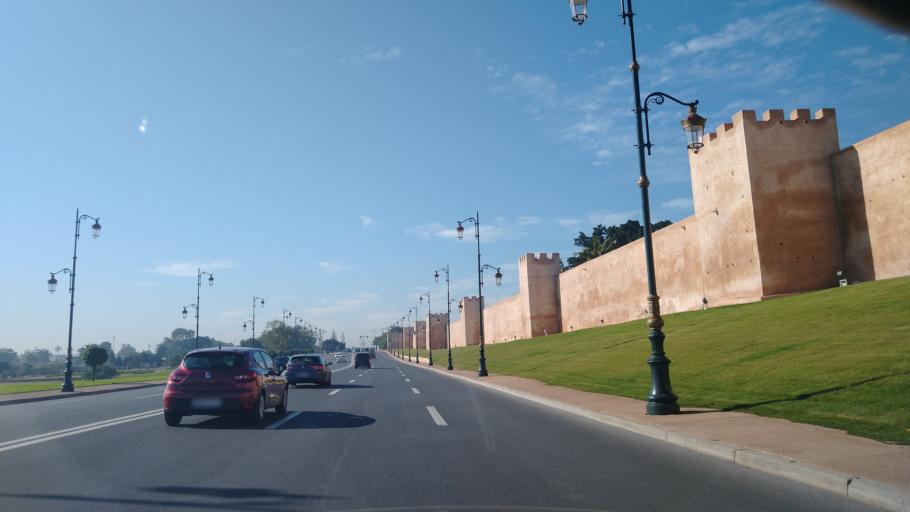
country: MA
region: Rabat-Sale-Zemmour-Zaer
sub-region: Rabat
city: Rabat
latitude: 34.0084
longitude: -6.8238
